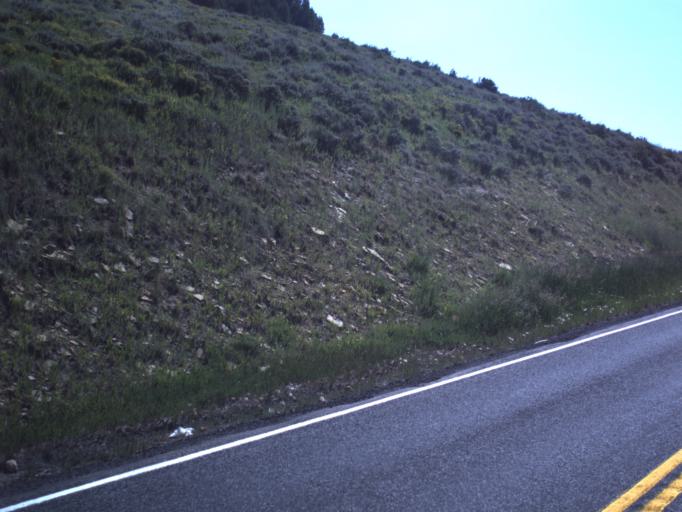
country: US
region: Utah
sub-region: Sanpete County
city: Fairview
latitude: 39.6849
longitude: -111.2443
